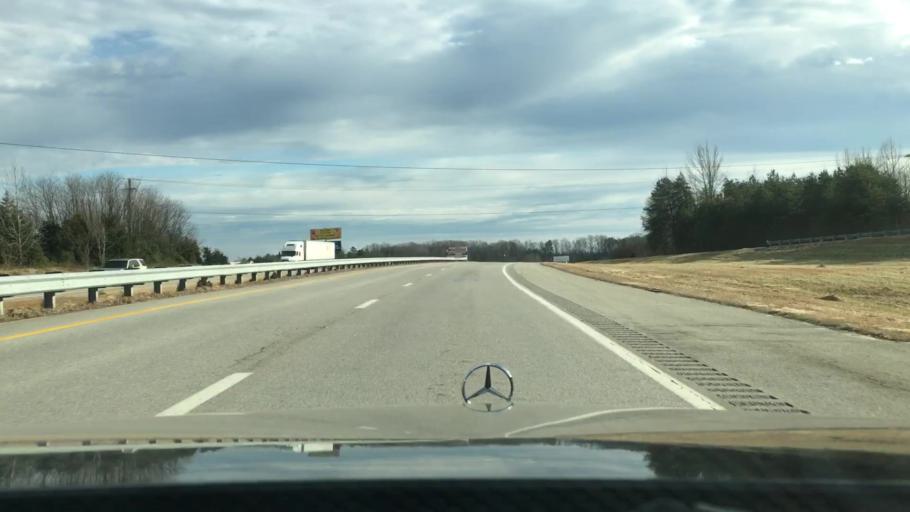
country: US
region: Virginia
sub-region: Pittsylvania County
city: Mount Hermon
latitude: 36.6974
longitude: -79.3630
